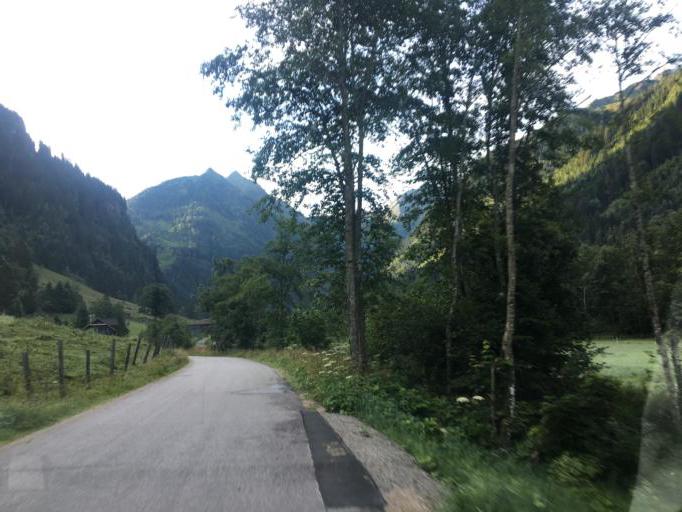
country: AT
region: Styria
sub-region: Politischer Bezirk Liezen
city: Haus
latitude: 47.3368
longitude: 13.7438
